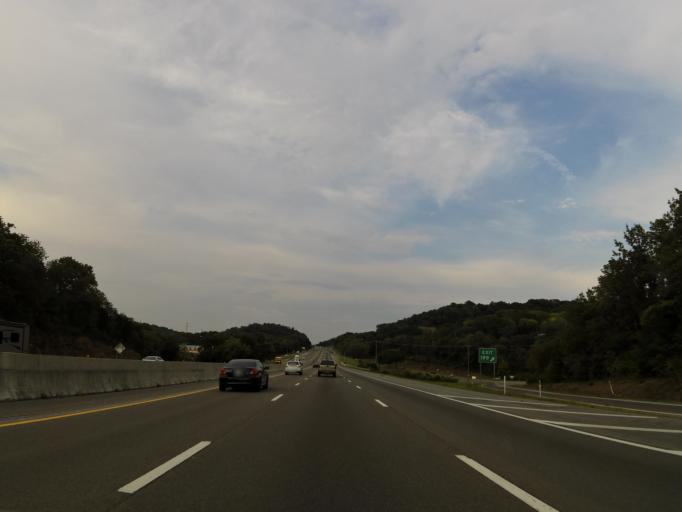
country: US
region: Tennessee
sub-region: Davidson County
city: Belle Meade
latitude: 36.1094
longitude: -86.9251
